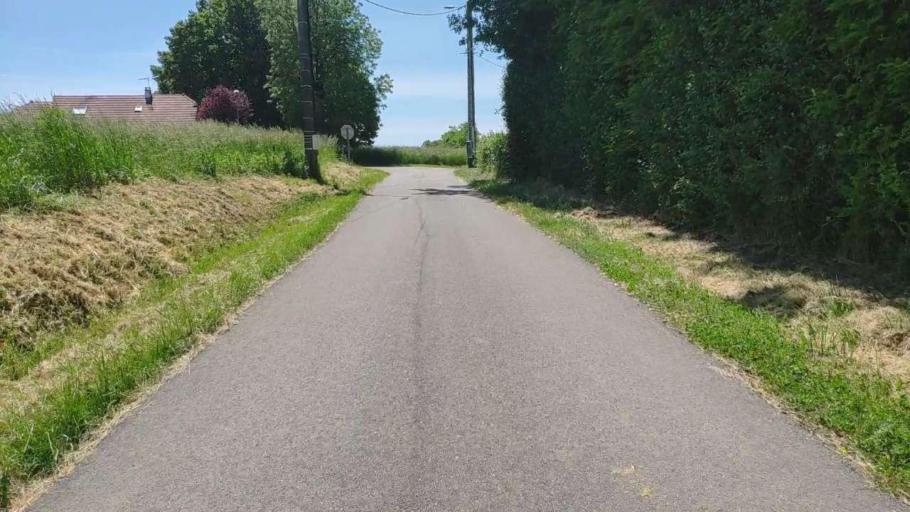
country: FR
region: Franche-Comte
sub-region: Departement du Jura
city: Bletterans
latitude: 46.7398
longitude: 5.4325
